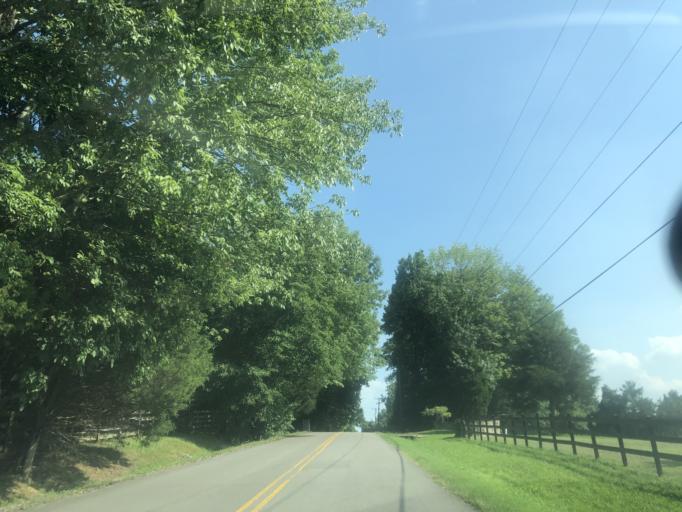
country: US
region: Tennessee
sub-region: Wilson County
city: Green Hill
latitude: 36.1443
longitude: -86.5954
